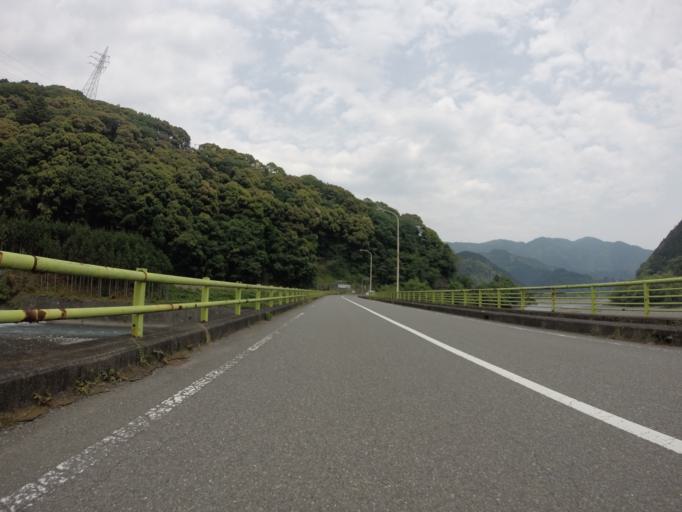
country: JP
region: Shizuoka
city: Shizuoka-shi
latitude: 35.1139
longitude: 138.3530
